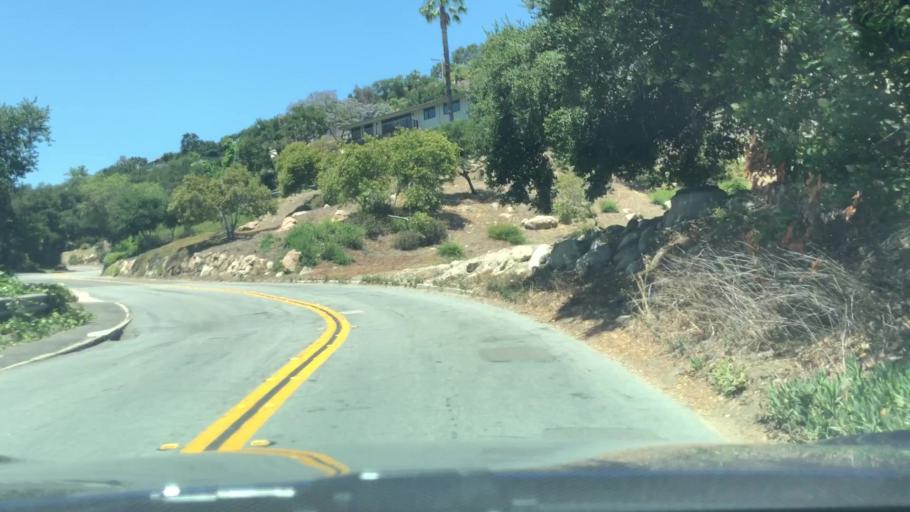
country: US
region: California
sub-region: Santa Barbara County
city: Santa Barbara
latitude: 34.4353
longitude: -119.6853
